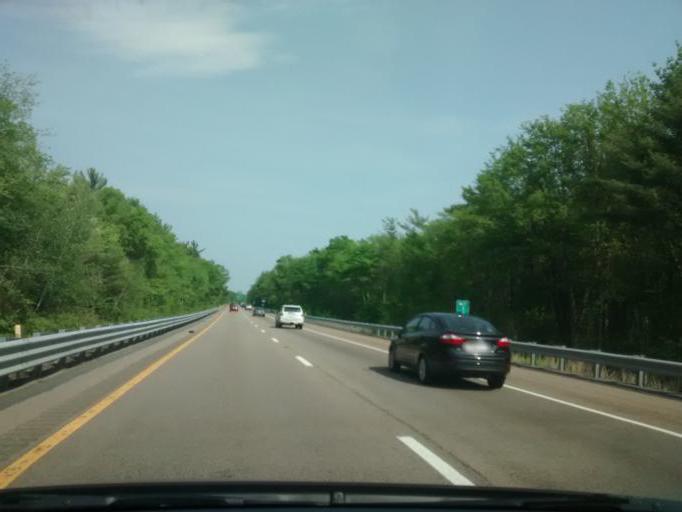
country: US
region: Massachusetts
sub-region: Plymouth County
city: West Wareham
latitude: 41.8104
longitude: -70.7826
